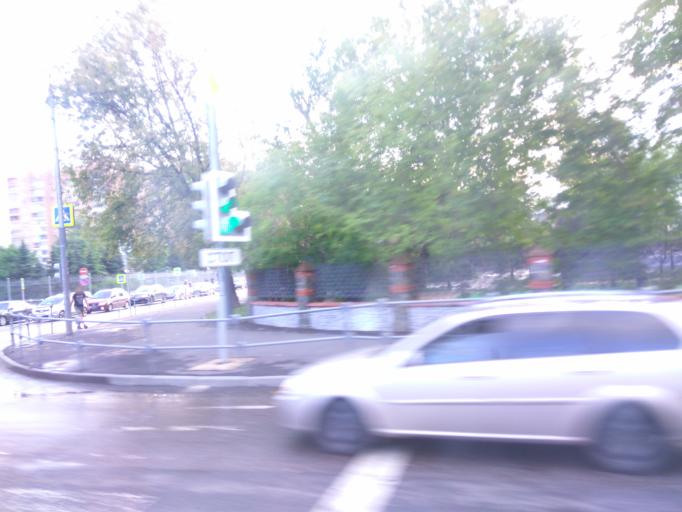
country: RU
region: Moskovskaya
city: Bogorodskoye
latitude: 55.8038
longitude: 37.7075
